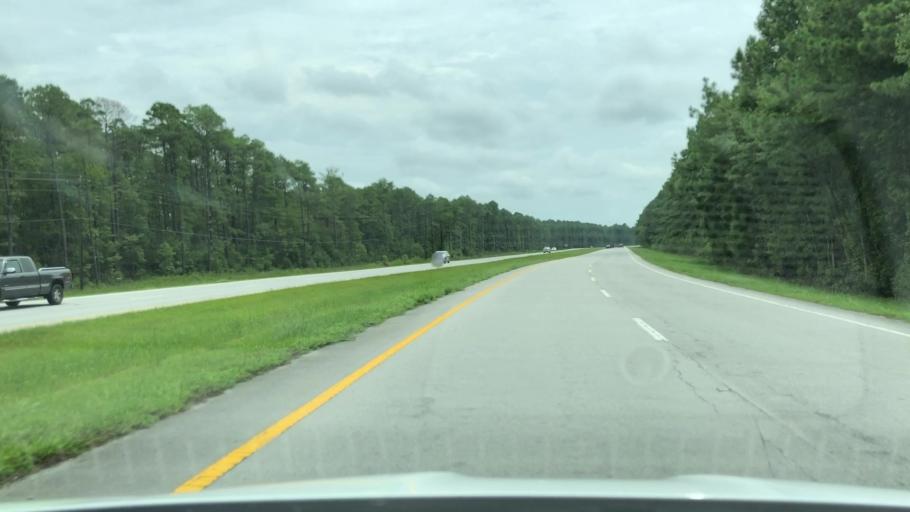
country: US
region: North Carolina
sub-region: Craven County
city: Havelock
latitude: 34.8507
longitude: -76.8883
